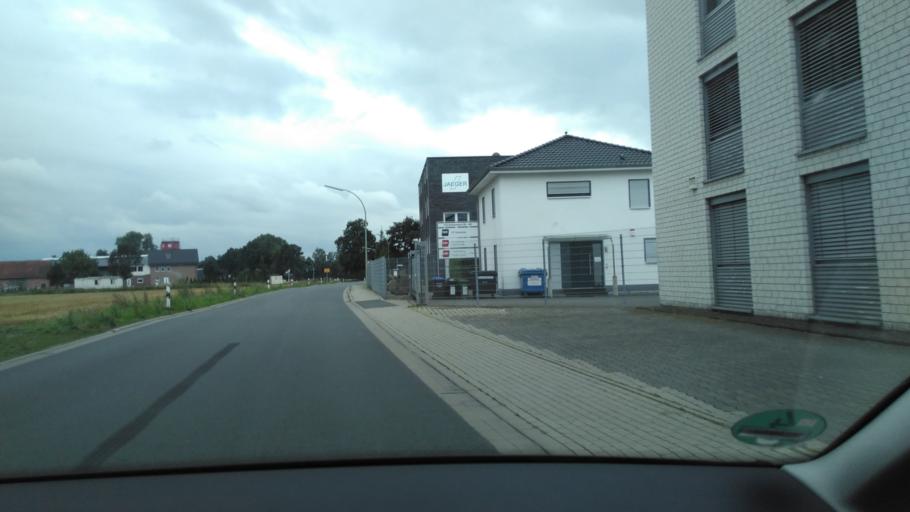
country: DE
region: North Rhine-Westphalia
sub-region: Regierungsbezirk Detmold
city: Verl
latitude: 51.8690
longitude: 8.4640
